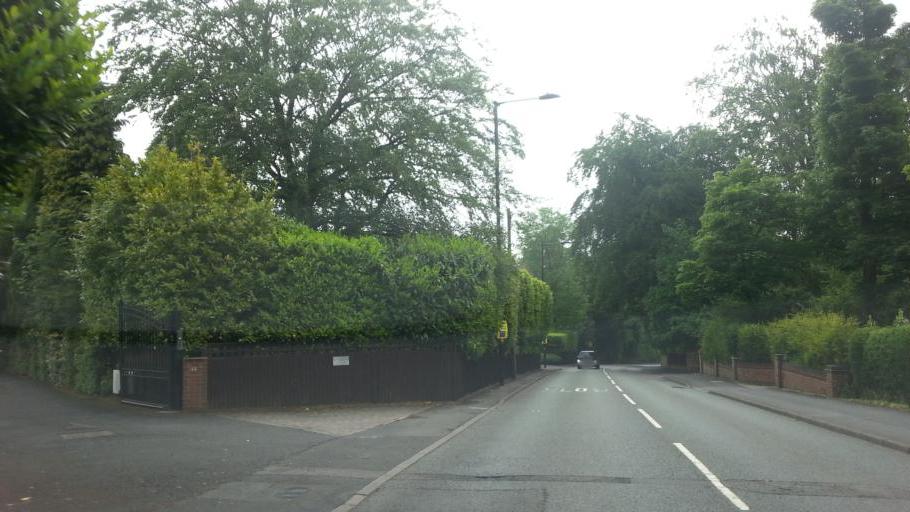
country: GB
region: England
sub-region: City and Borough of Birmingham
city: Sutton Coldfield
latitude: 52.5839
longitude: -1.8362
